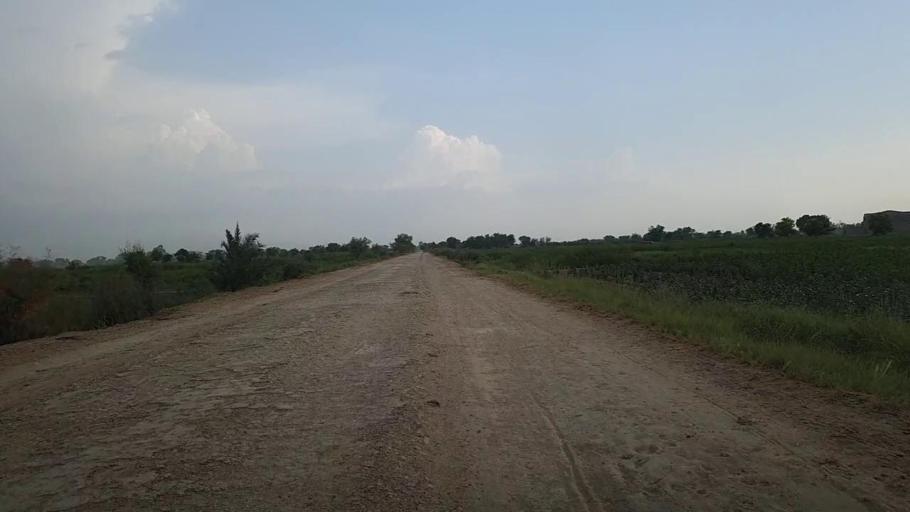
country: PK
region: Sindh
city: Khanpur
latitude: 27.8624
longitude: 69.4871
